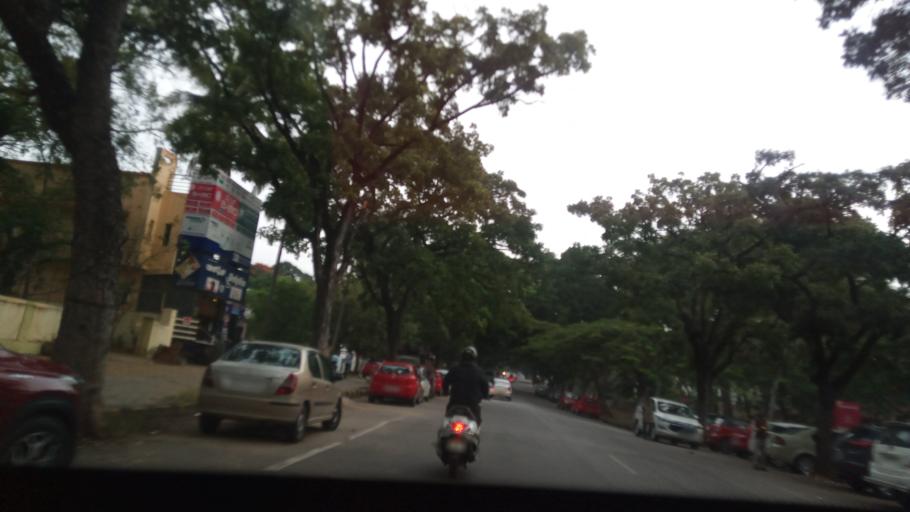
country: IN
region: Karnataka
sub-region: Mysore
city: Mysore
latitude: 12.3280
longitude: 76.6313
